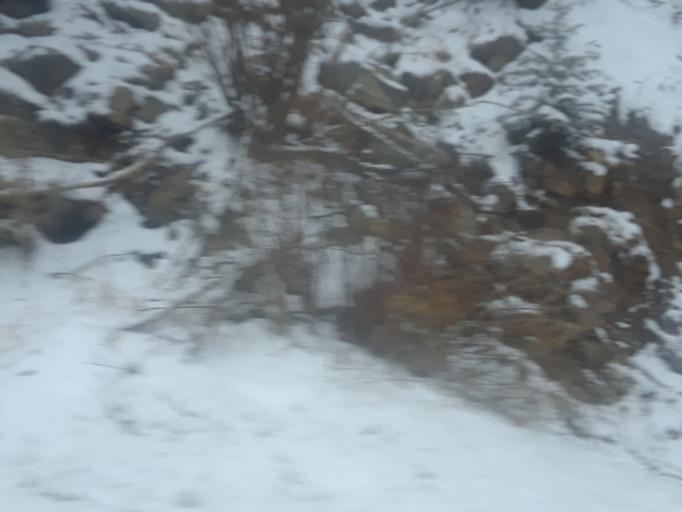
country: US
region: Colorado
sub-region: Boulder County
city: Coal Creek
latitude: 39.9244
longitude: -105.4204
